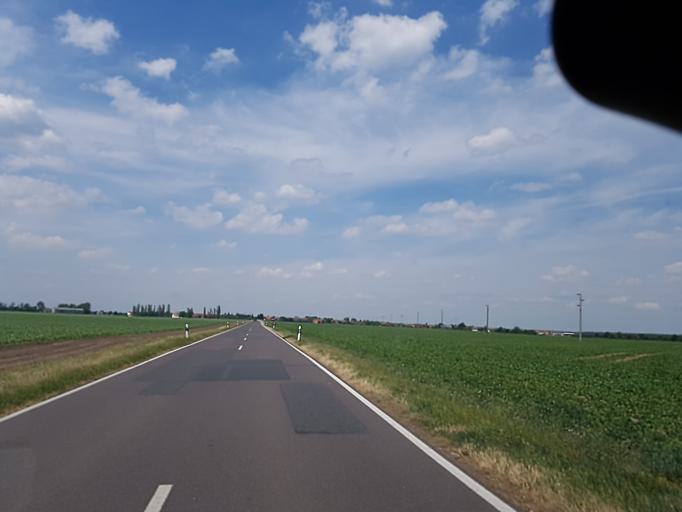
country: DE
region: Brandenburg
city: Gorzke
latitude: 52.1324
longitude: 12.3268
